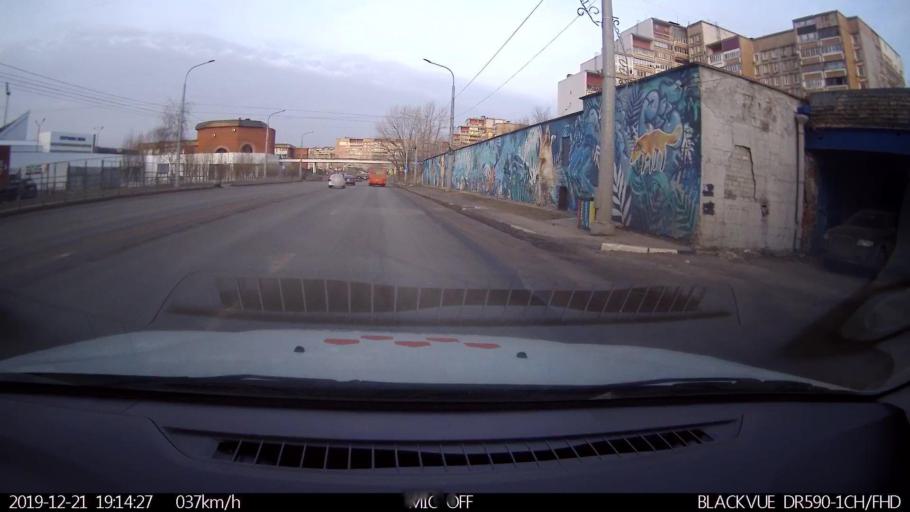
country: RU
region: Nizjnij Novgorod
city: Nizhniy Novgorod
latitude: 56.3405
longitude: 43.9424
